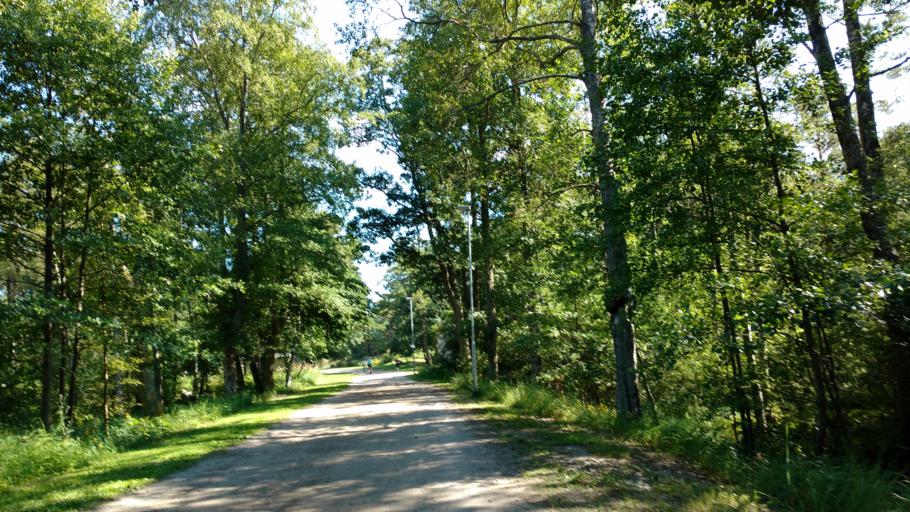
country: FI
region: Varsinais-Suomi
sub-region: Aboland-Turunmaa
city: Dragsfjaerd
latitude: 59.8077
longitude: 22.3327
